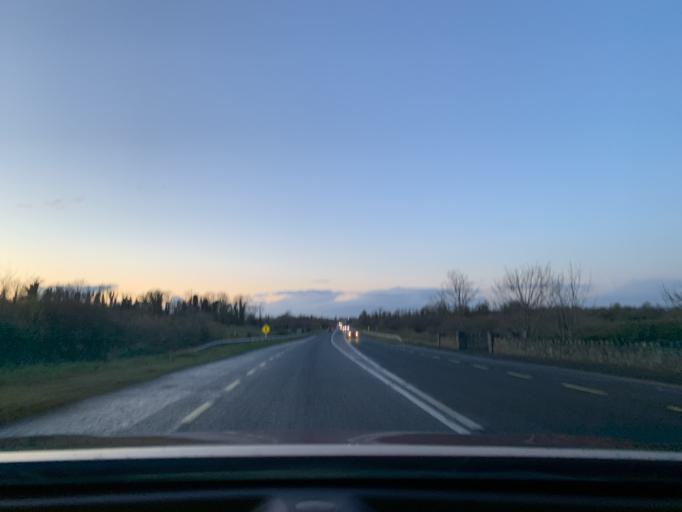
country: IE
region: Connaught
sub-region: County Leitrim
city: Carrick-on-Shannon
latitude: 53.9368
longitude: -8.0556
